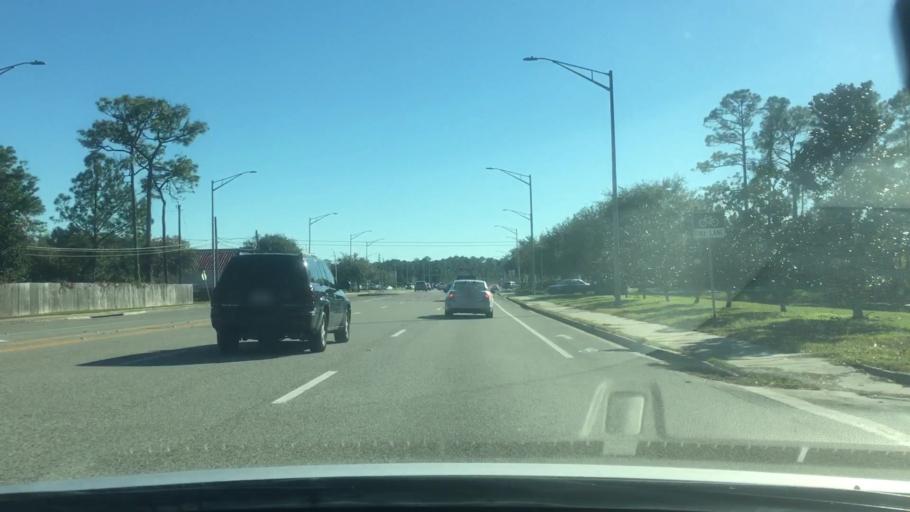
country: US
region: Florida
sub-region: Duval County
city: Jacksonville Beach
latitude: 30.2898
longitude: -81.4590
